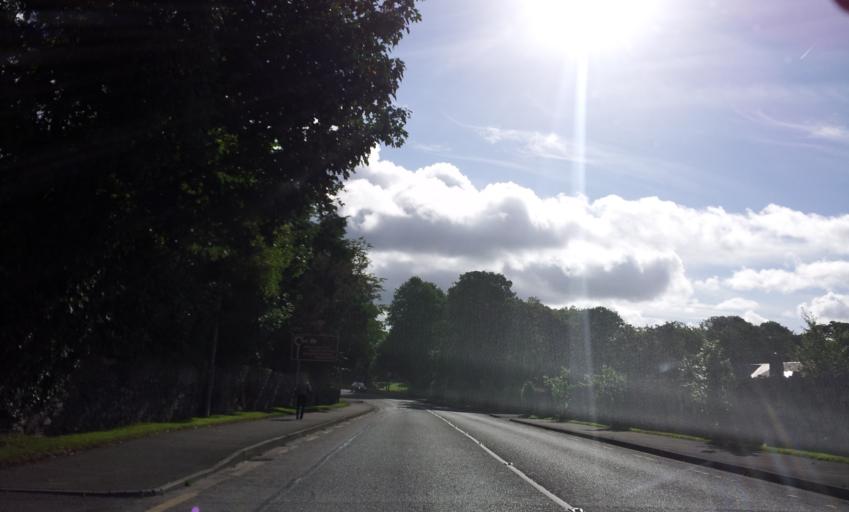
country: IE
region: Munster
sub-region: Ciarrai
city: Cill Airne
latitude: 52.0677
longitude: -9.5264
